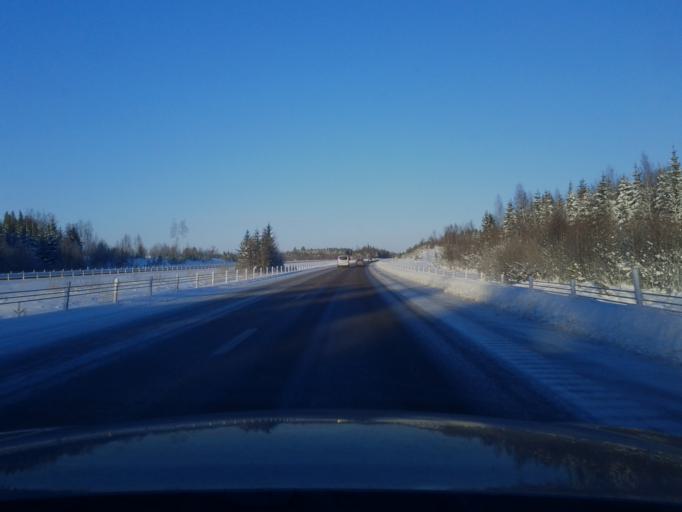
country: SE
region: Uppsala
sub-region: Tierps Kommun
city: Tierp
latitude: 60.3878
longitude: 17.4781
